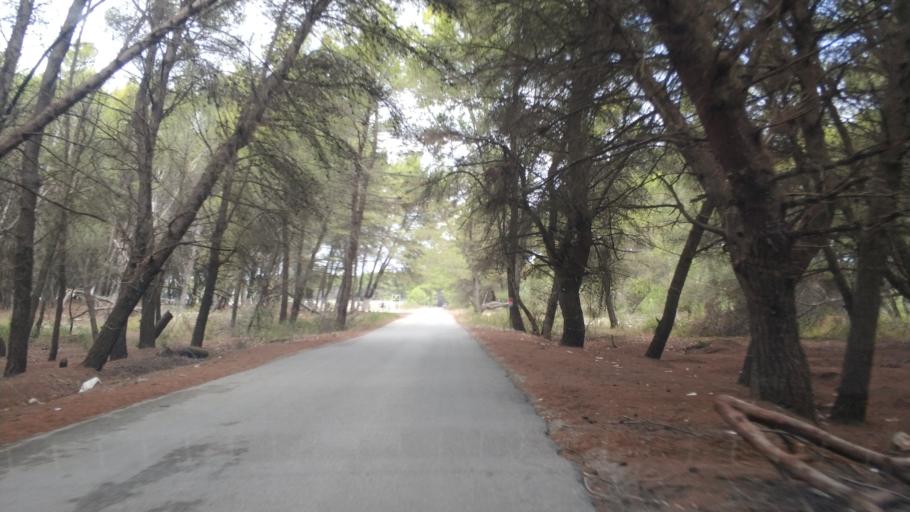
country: AL
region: Vlore
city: Vlore
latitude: 40.4900
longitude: 19.4397
